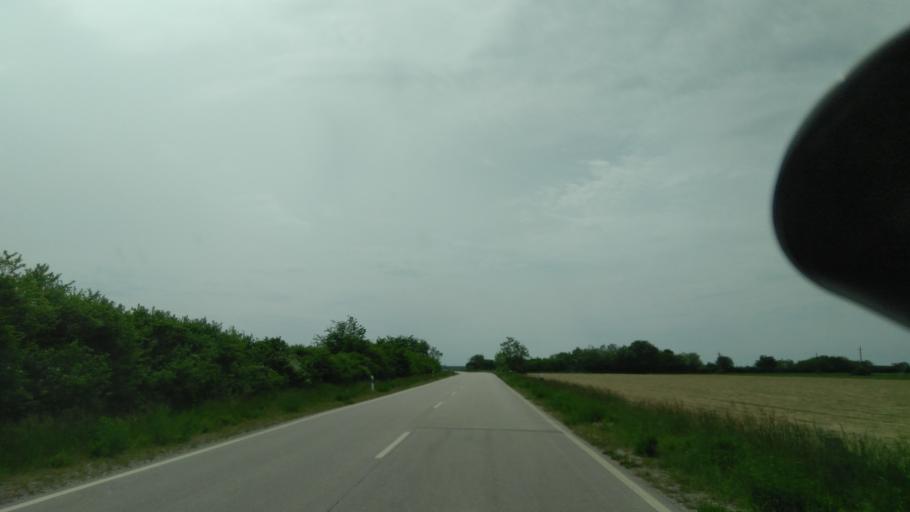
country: HU
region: Bekes
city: Mehkerek
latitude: 46.8675
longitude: 21.4985
